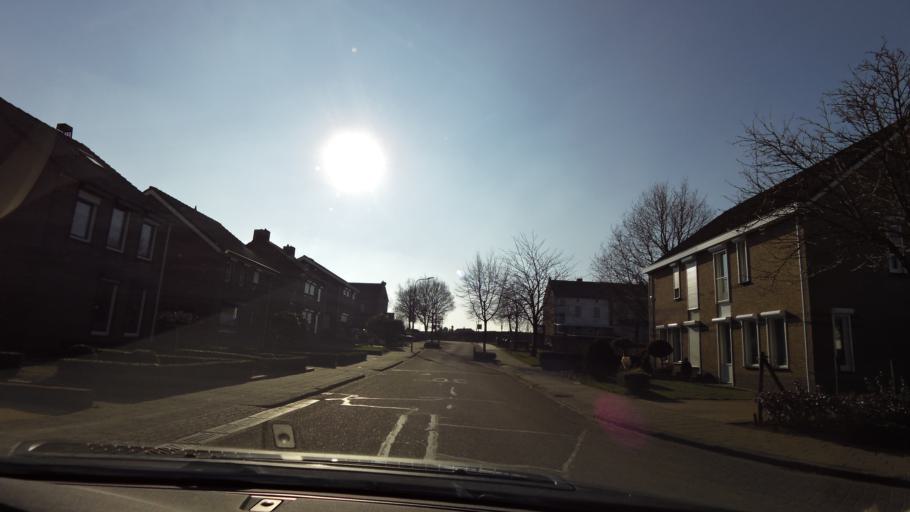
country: NL
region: Limburg
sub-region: Gemeente Simpelveld
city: Simpelveld
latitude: 50.8173
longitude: 6.0019
